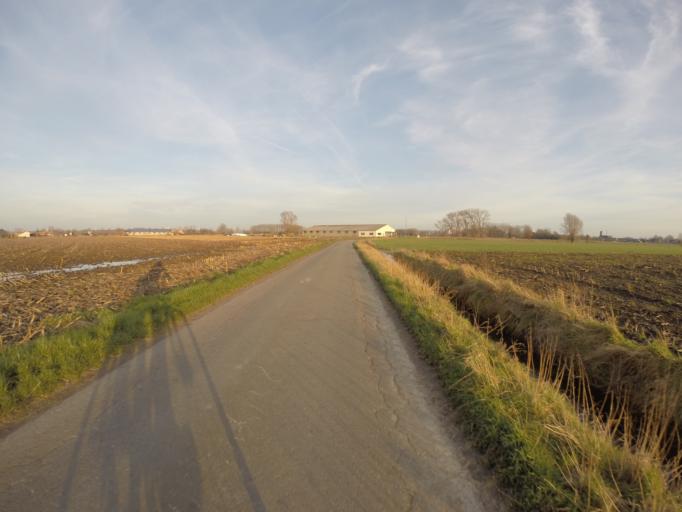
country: BE
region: Flanders
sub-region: Provincie Oost-Vlaanderen
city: Knesselare
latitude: 51.1159
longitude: 3.4224
